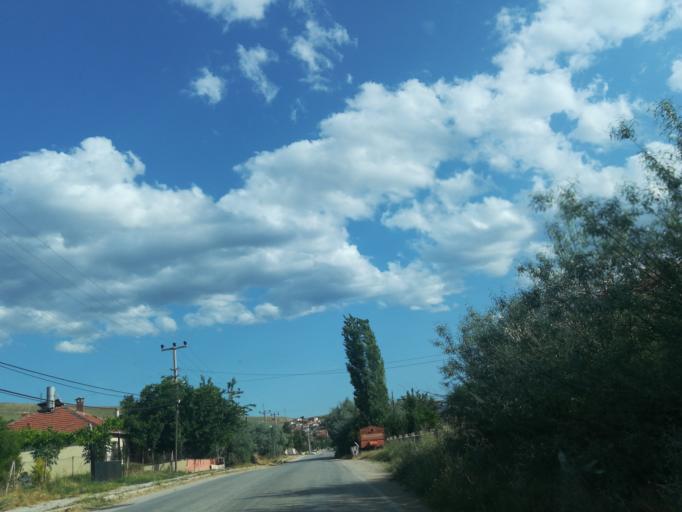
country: TR
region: Afyonkarahisar
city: Dinar
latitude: 38.0817
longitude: 30.1672
